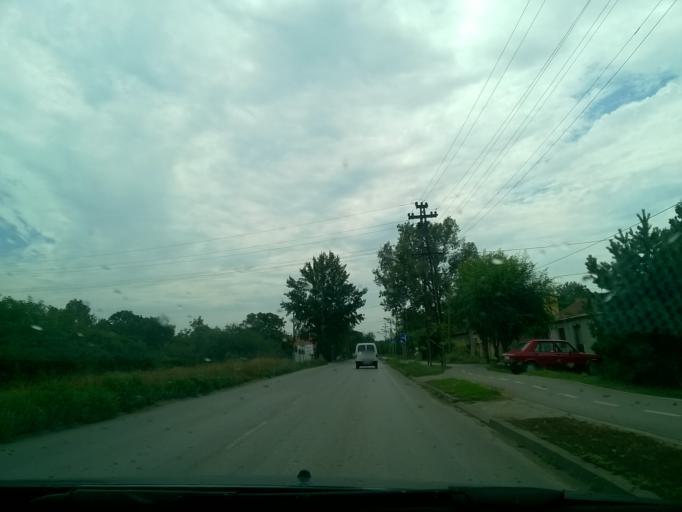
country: RS
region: Autonomna Pokrajina Vojvodina
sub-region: Srednjebanatski Okrug
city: Zrenjanin
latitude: 45.3933
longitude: 20.4068
